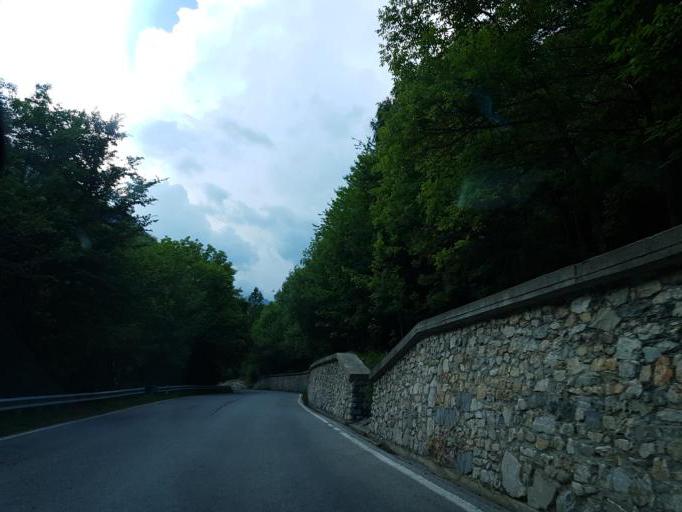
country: IT
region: Piedmont
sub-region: Provincia di Cuneo
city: Prazzo Superiore
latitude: 44.4794
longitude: 7.0500
